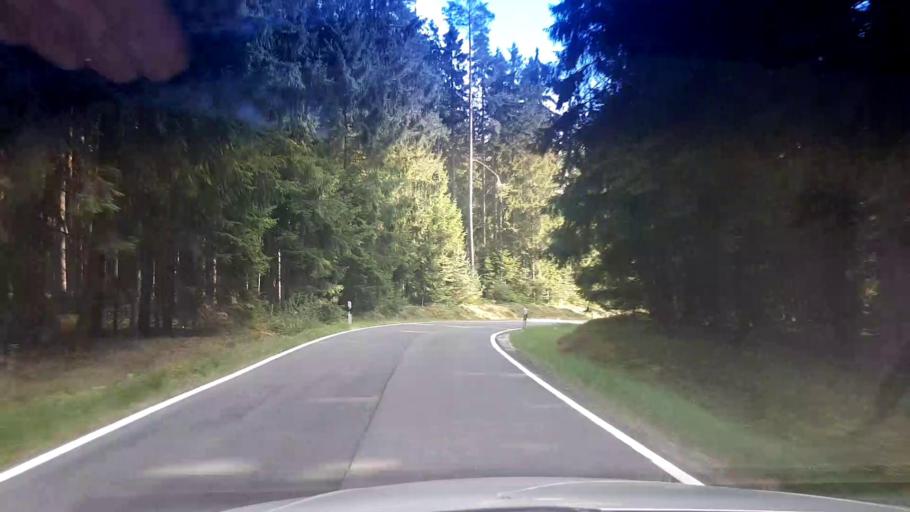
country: DE
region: Bavaria
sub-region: Upper Palatinate
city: Neualbenreuth
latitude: 49.9266
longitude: 12.4067
